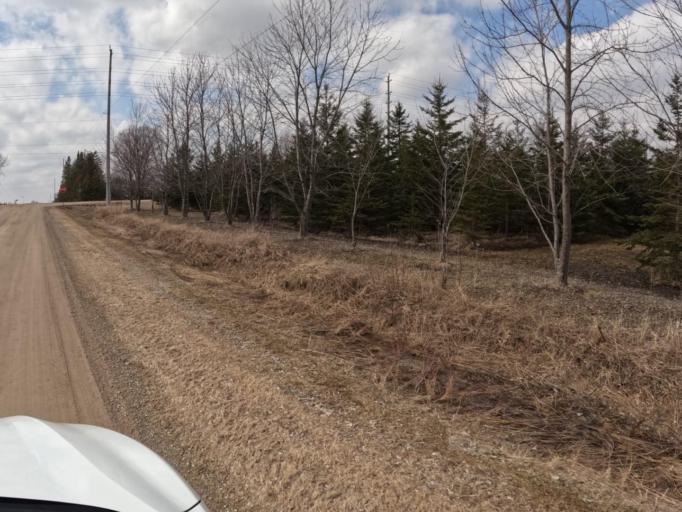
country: CA
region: Ontario
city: Shelburne
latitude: 44.0176
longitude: -80.3114
